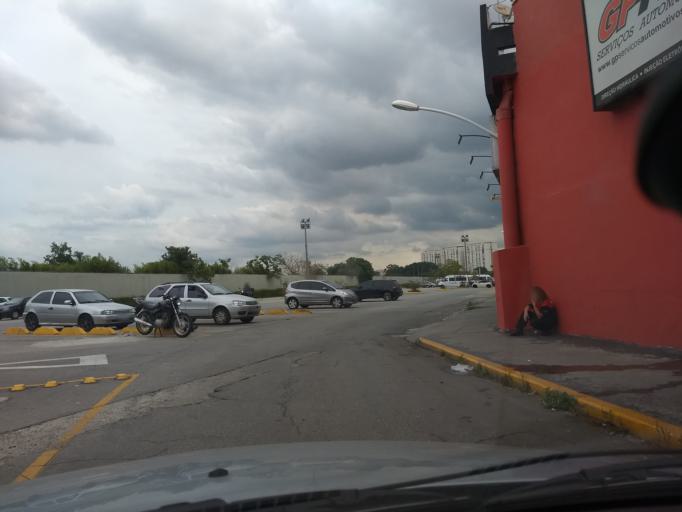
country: BR
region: Sao Paulo
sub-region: Sao Paulo
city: Sao Paulo
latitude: -23.5214
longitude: -46.5977
